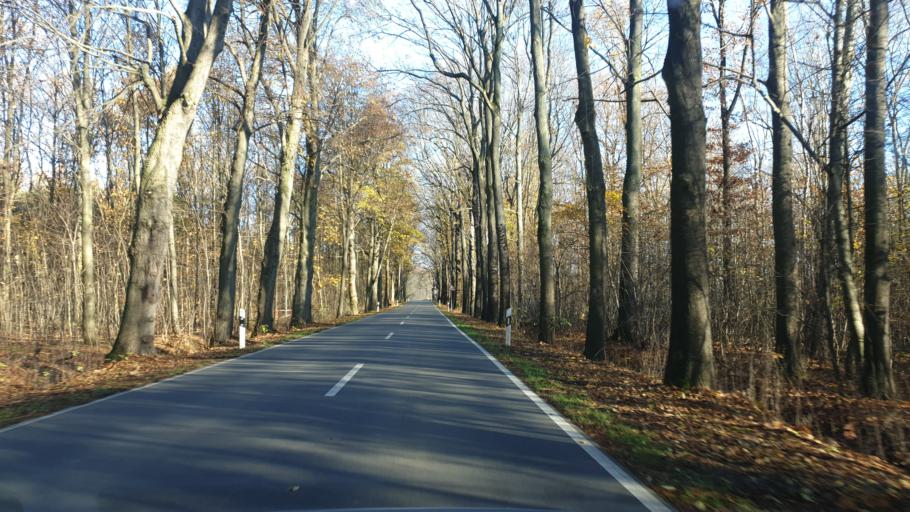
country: DE
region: Saxony-Anhalt
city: Wetterzeube
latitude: 51.0262
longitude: 12.0178
